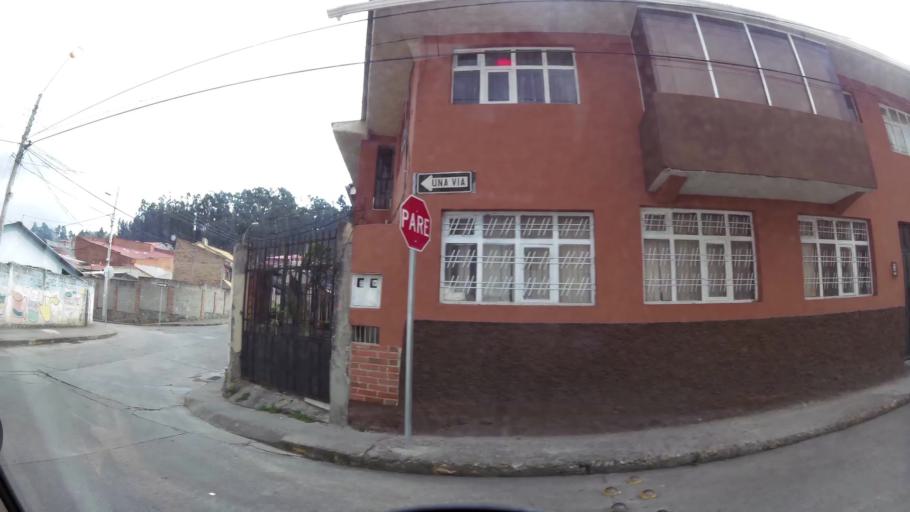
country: EC
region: Azuay
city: Cuenca
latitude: -2.8898
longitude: -79.0170
